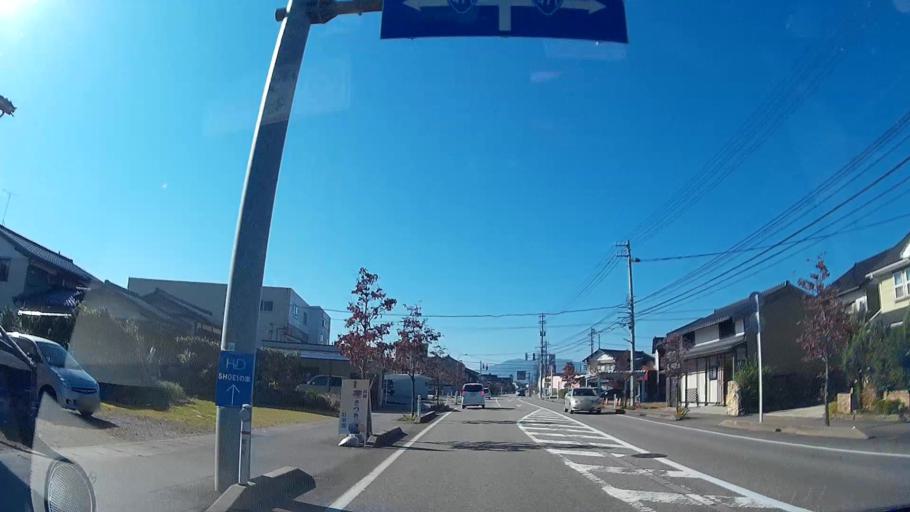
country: JP
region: Toyama
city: Nanto-shi
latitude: 36.5963
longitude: 136.9252
